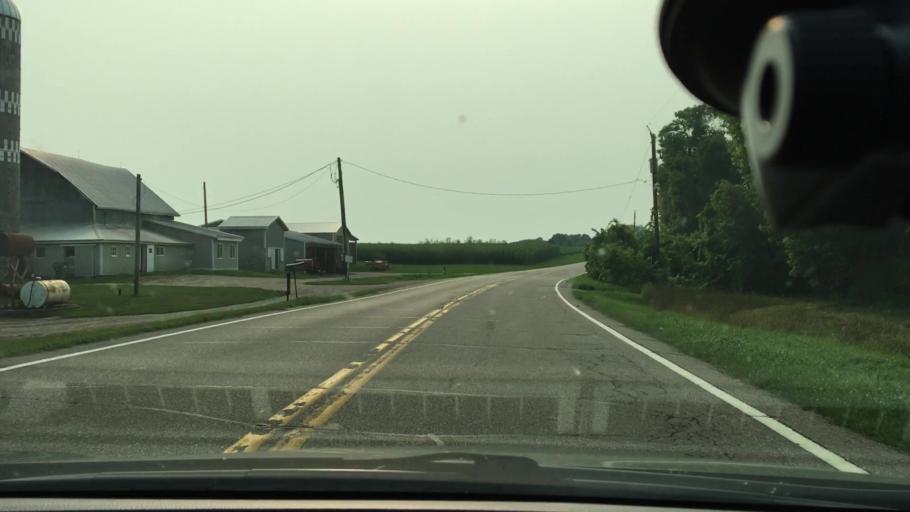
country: US
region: Minnesota
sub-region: Hennepin County
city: Dayton
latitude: 45.2230
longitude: -93.4785
